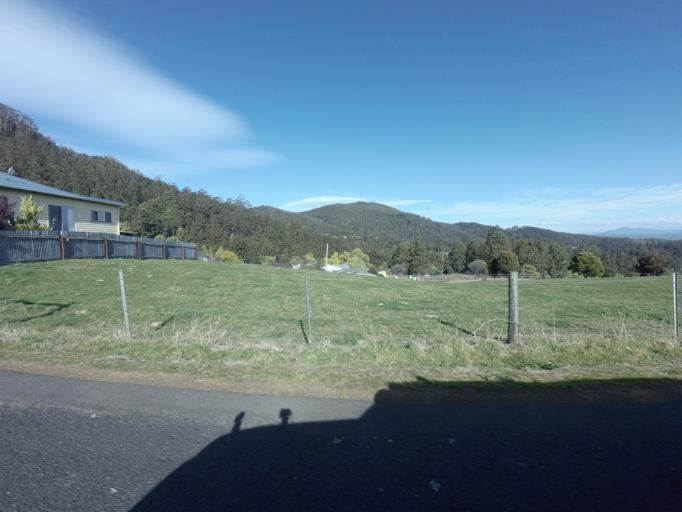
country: AU
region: Tasmania
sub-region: Kingborough
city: Kettering
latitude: -43.1703
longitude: 147.1737
